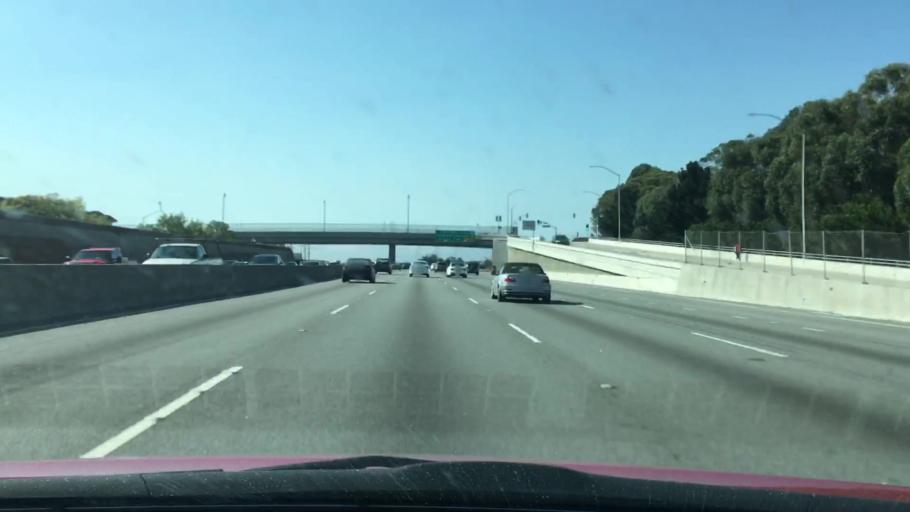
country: US
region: California
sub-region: San Mateo County
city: San Mateo
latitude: 37.5824
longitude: -122.3256
